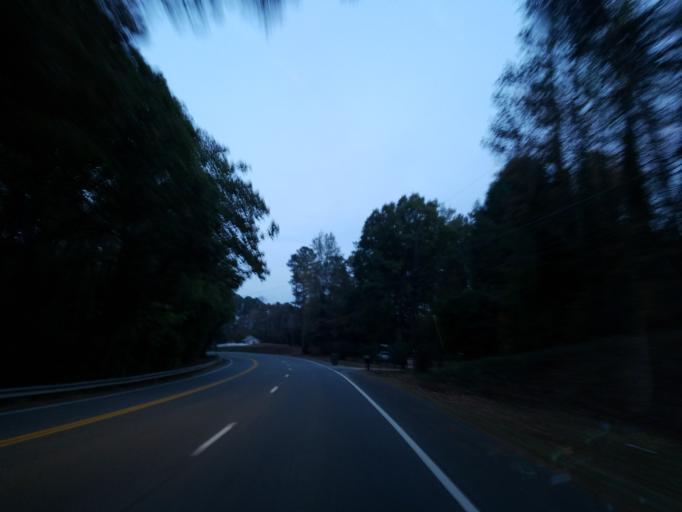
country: US
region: Georgia
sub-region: Pickens County
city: Jasper
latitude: 34.5009
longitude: -84.4782
